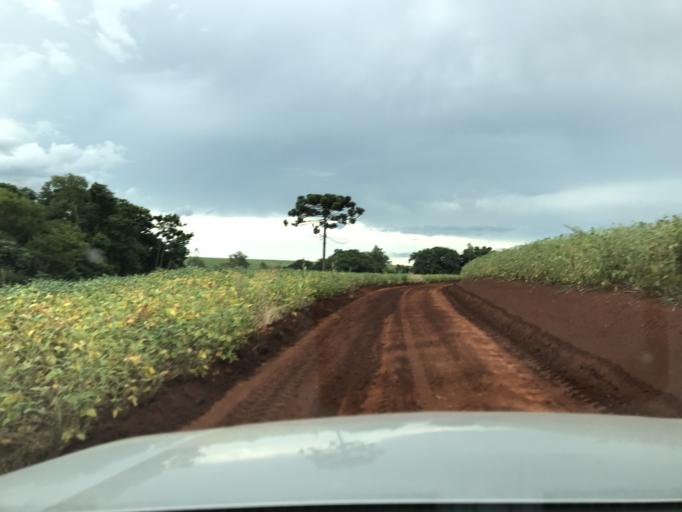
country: BR
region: Parana
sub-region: Palotina
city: Palotina
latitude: -24.2694
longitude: -53.7713
